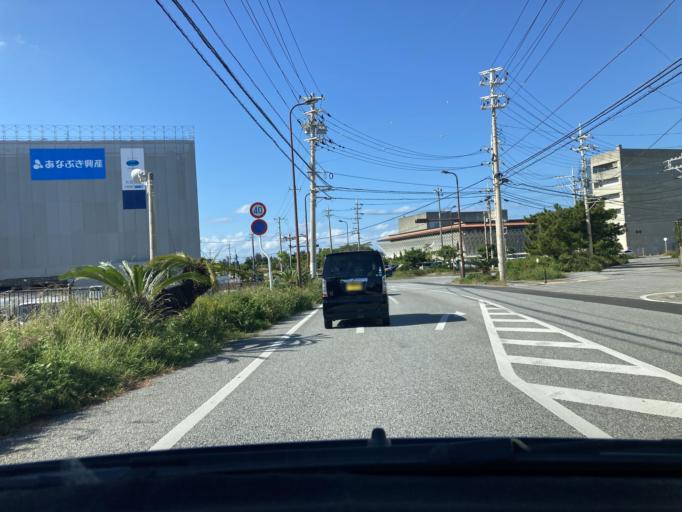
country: JP
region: Okinawa
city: Naha-shi
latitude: 26.2442
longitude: 127.6900
